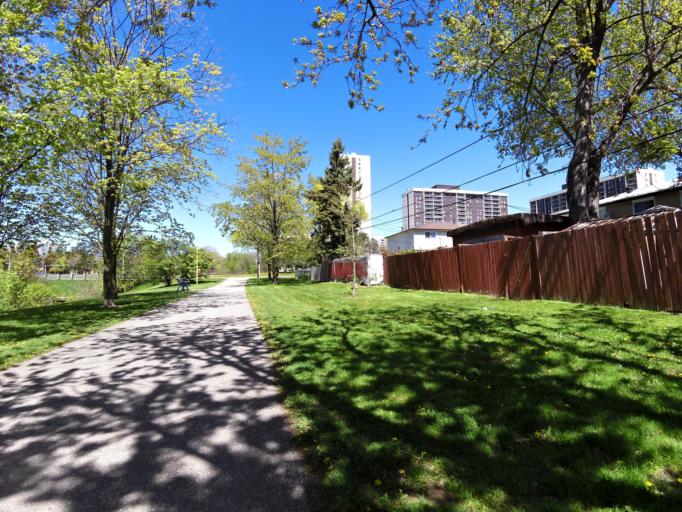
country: CA
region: Ontario
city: Brampton
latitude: 43.7168
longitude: -79.7138
